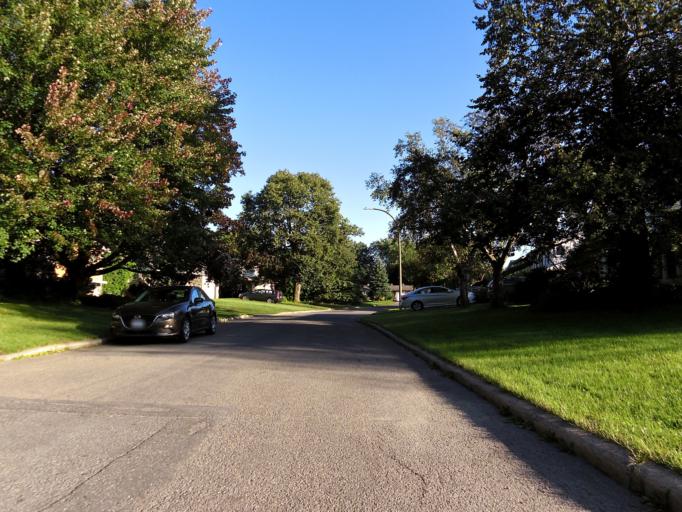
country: CA
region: Ontario
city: Ottawa
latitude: 45.3542
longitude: -75.7230
